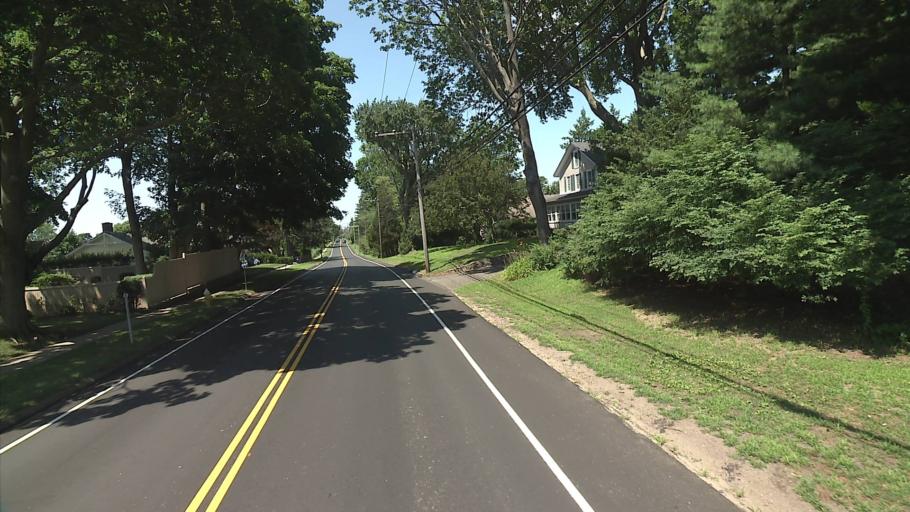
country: US
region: Connecticut
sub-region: Middlesex County
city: Old Saybrook Center
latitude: 41.2839
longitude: -72.3576
